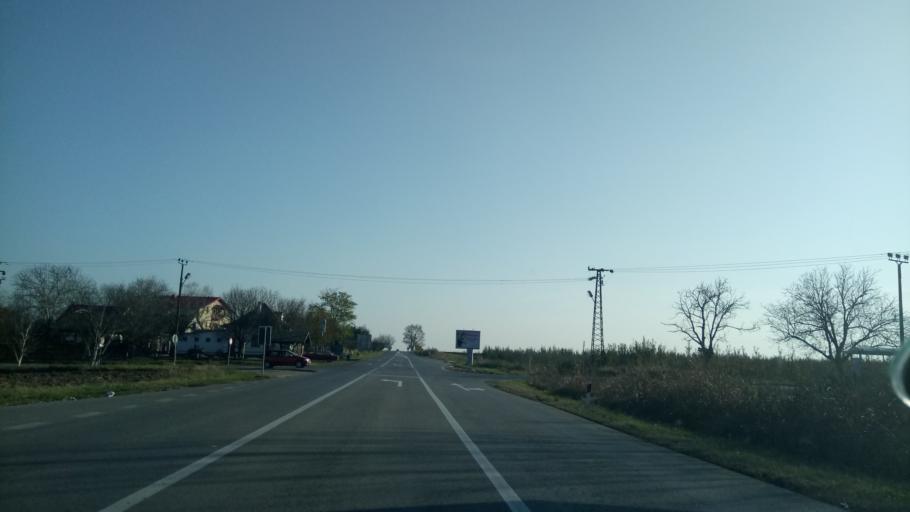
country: RS
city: Cortanovci
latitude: 45.1103
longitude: 20.0262
